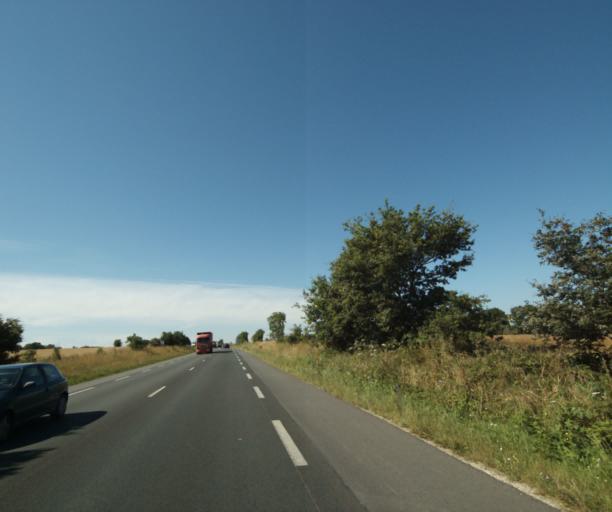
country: FR
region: Pays de la Loire
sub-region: Departement de la Mayenne
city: Bonchamp-les-Laval
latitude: 48.0658
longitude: -0.7328
